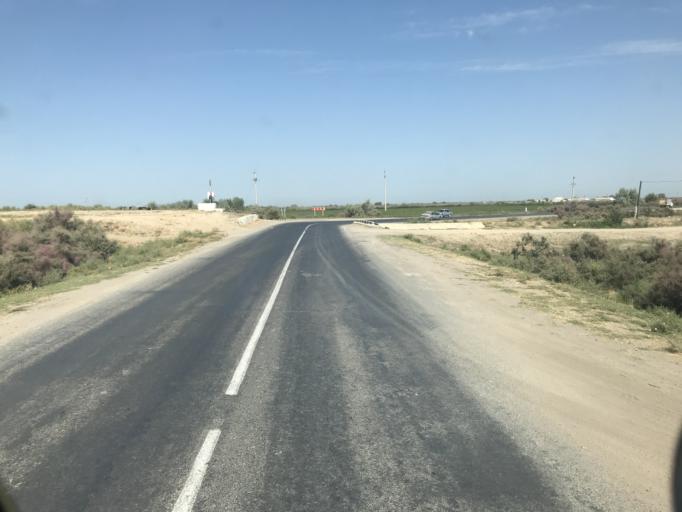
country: KZ
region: Ongtustik Qazaqstan
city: Myrzakent
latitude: 40.6797
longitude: 68.5328
